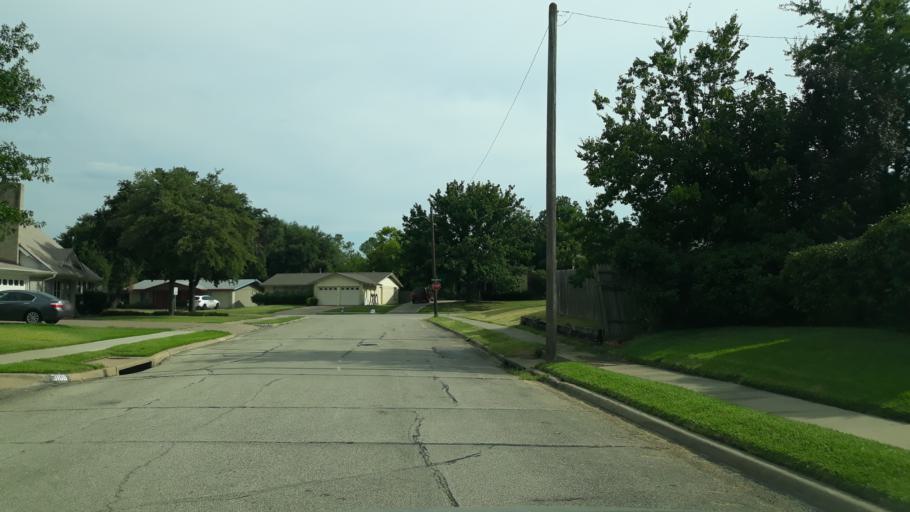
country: US
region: Texas
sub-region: Dallas County
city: Irving
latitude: 32.8494
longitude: -96.9898
